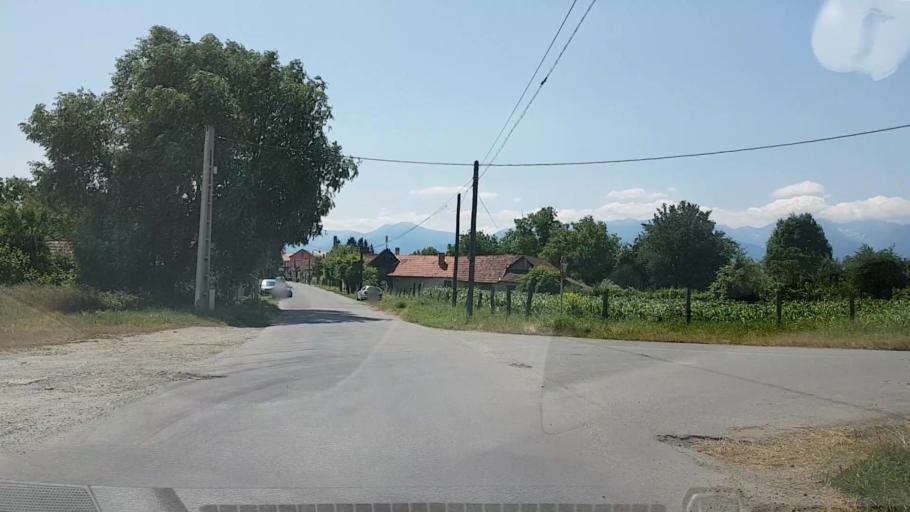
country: RO
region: Brasov
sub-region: Comuna Voila
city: Voila
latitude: 45.8213
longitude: 24.8386
